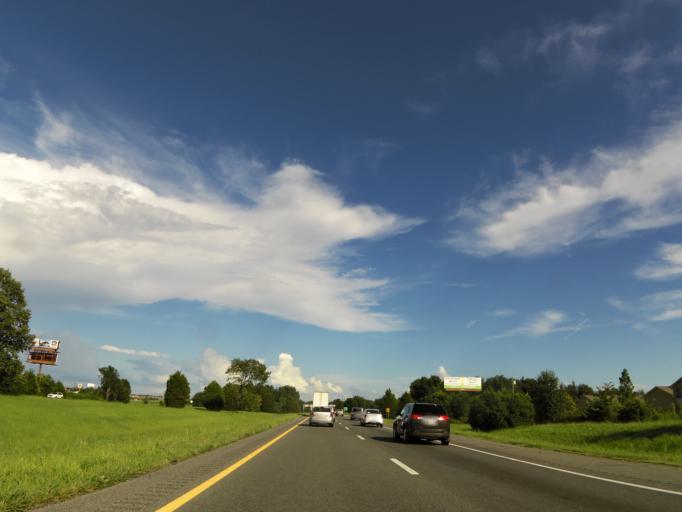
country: US
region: Tennessee
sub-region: Montgomery County
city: Clarksville
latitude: 36.6326
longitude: -87.3238
